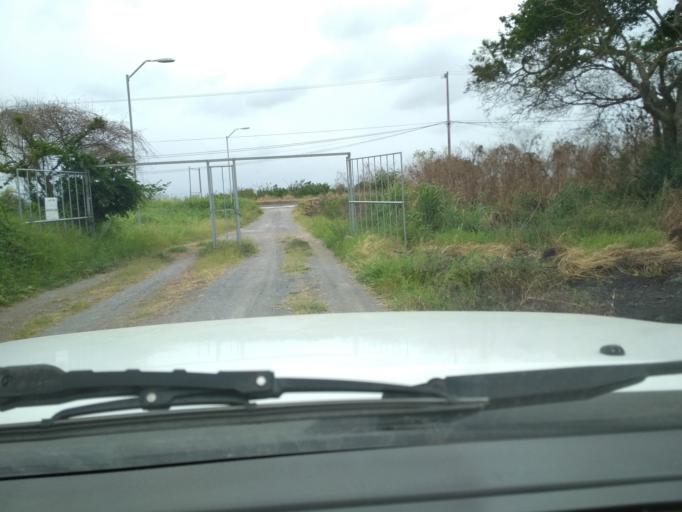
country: MX
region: Veracruz
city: Paso del Toro
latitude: 19.0465
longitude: -96.1343
